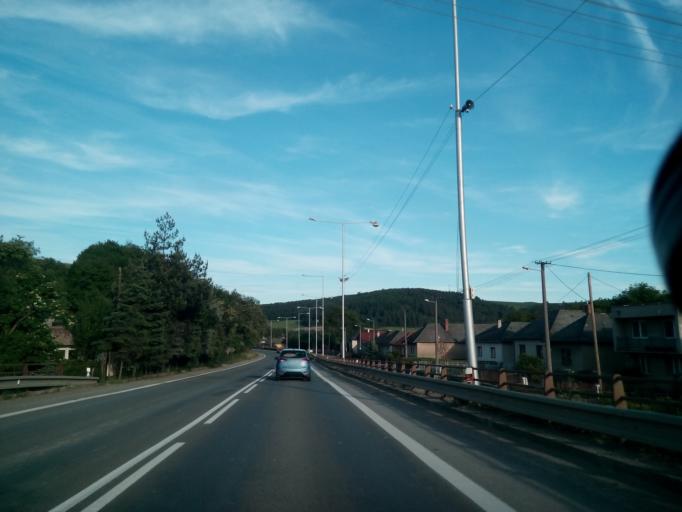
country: SK
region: Presovsky
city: Sabinov
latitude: 49.0066
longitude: 21.0699
